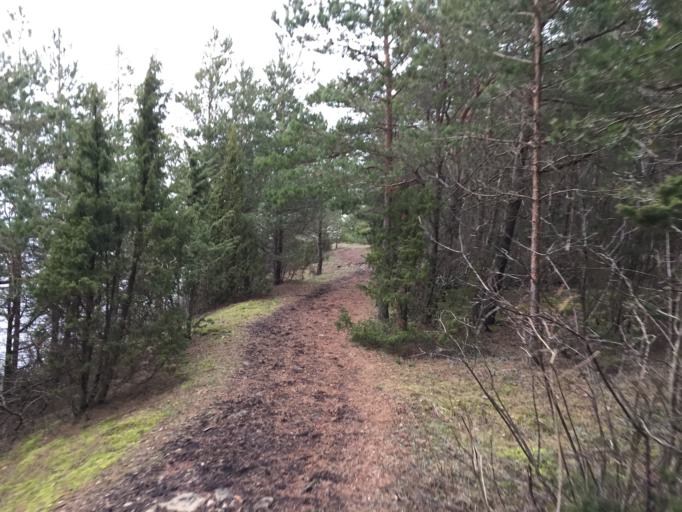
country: EE
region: Saare
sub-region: Kuressaare linn
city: Kuressaare
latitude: 58.5678
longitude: 22.2858
